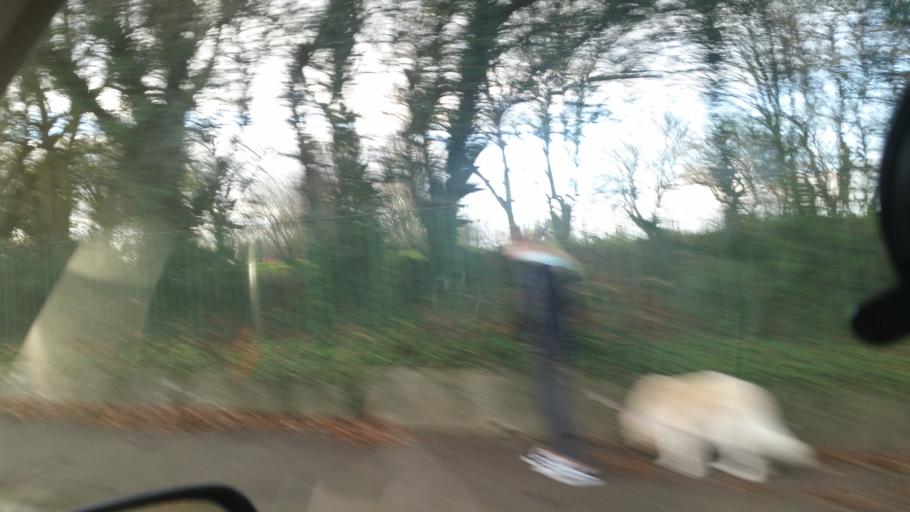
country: IE
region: Leinster
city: Beaumont
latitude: 53.3867
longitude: -6.2392
